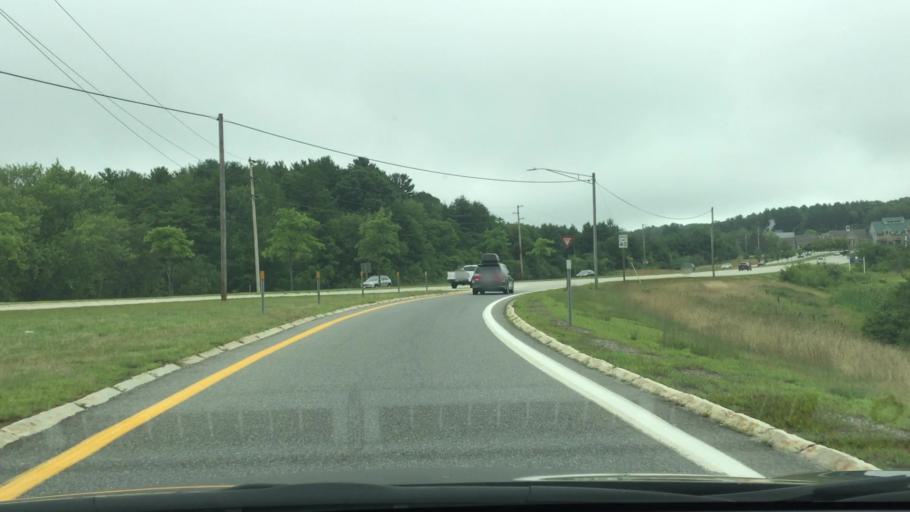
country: US
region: Maine
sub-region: York County
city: York Harbor
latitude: 43.1557
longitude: -70.6641
